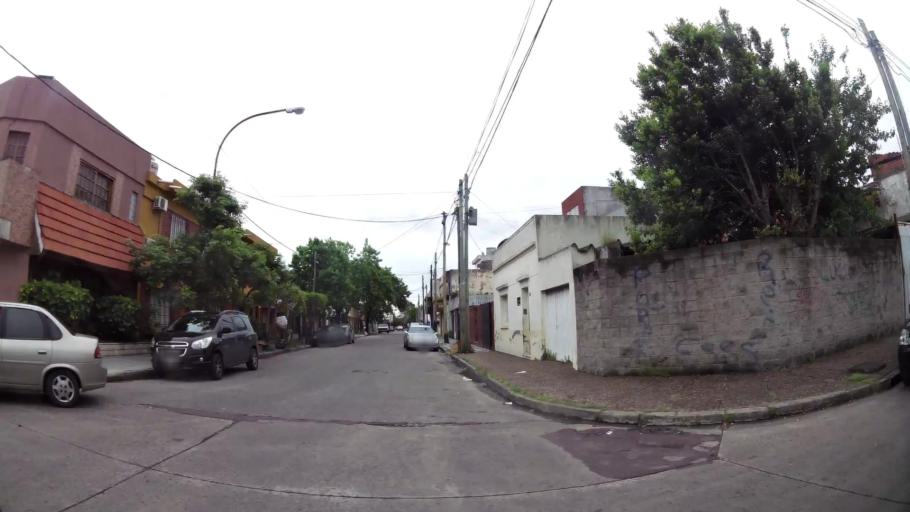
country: AR
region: Buenos Aires
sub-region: Partido de Lanus
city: Lanus
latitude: -34.7011
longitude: -58.3852
